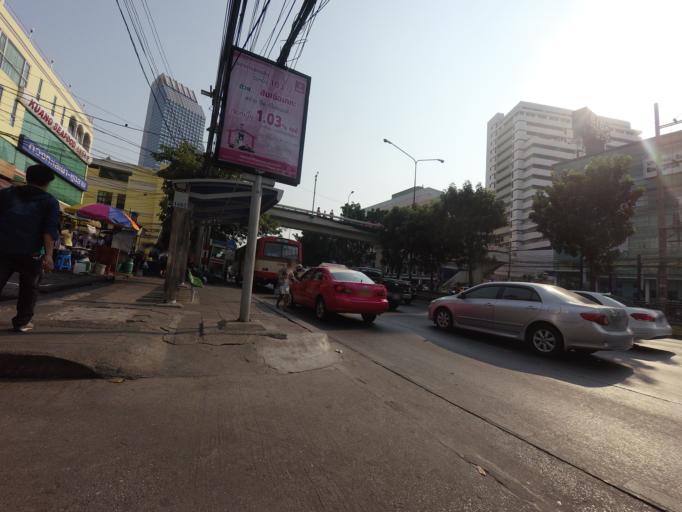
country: TH
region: Bangkok
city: Huai Khwang
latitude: 13.7730
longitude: 100.5735
